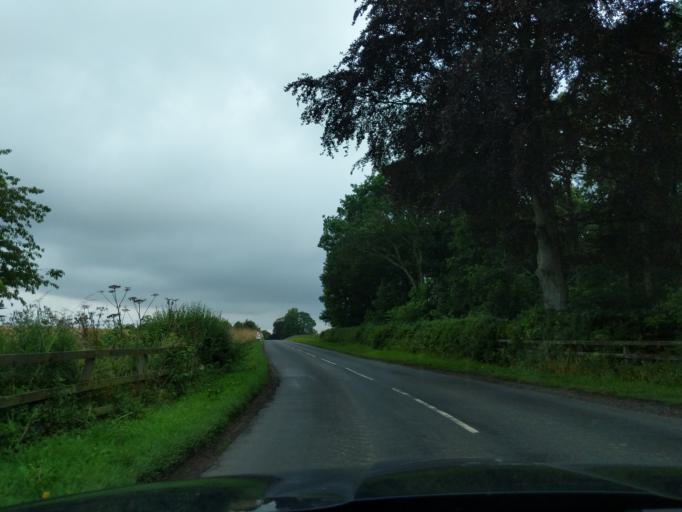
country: GB
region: England
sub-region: Northumberland
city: Ford
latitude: 55.6429
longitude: -2.1085
